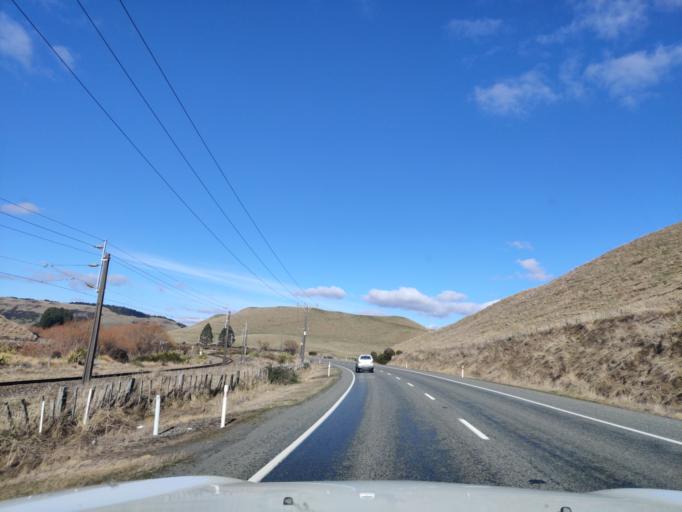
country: NZ
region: Manawatu-Wanganui
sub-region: Ruapehu District
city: Waiouru
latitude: -39.5043
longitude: 175.6741
